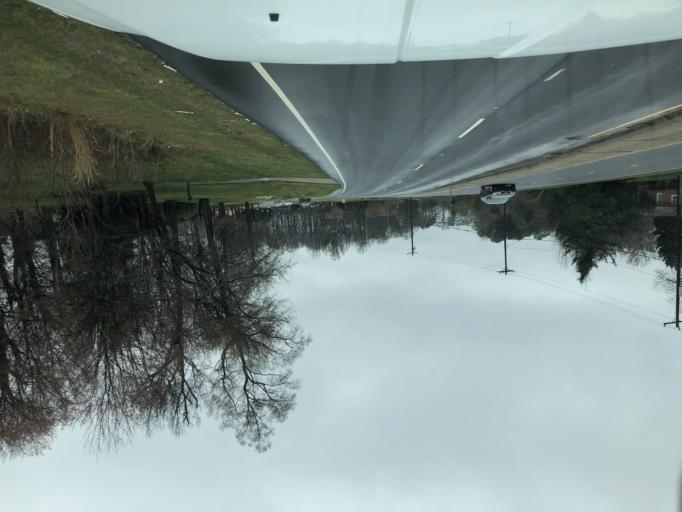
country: US
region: North Carolina
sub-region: Mecklenburg County
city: Huntersville
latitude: 35.3543
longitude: -80.8674
